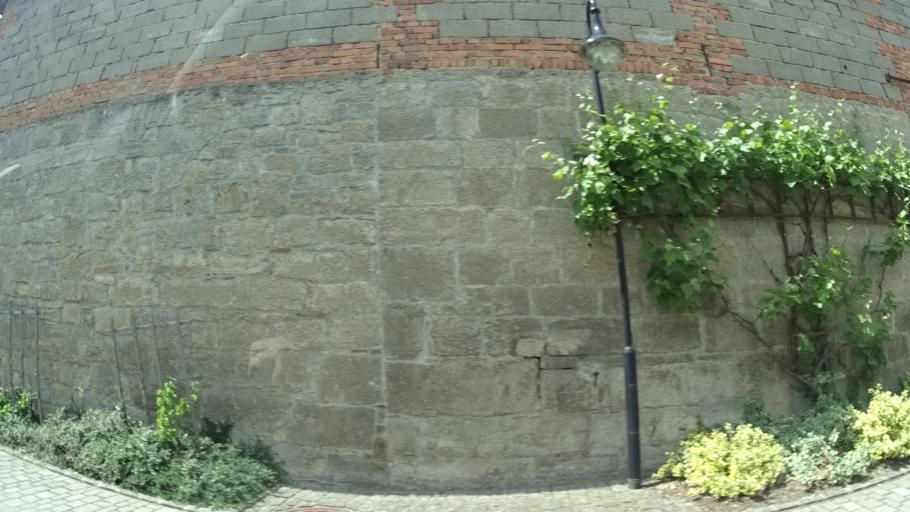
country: DE
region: Bavaria
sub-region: Regierungsbezirk Unterfranken
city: Salz
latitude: 50.3087
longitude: 10.2078
